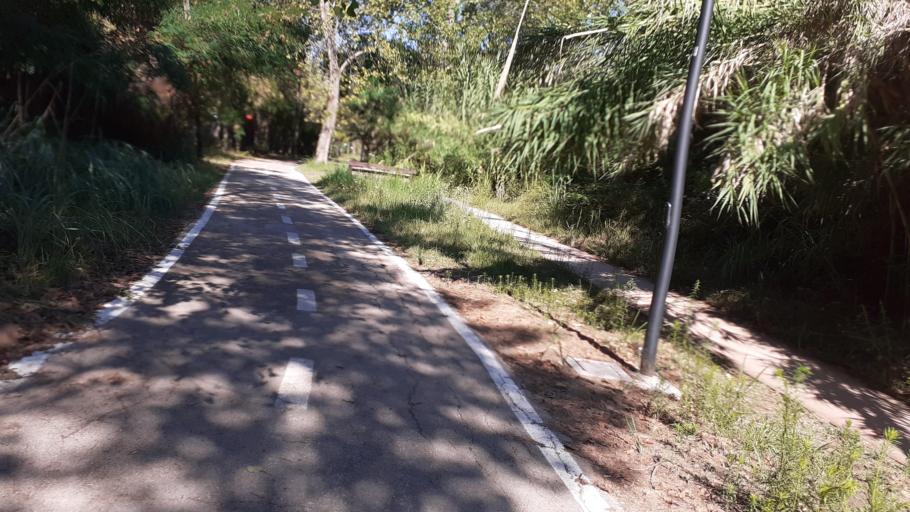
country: IT
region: Abruzzo
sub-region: Provincia di Chieti
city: Marina di Vasto
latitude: 42.0818
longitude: 14.7458
